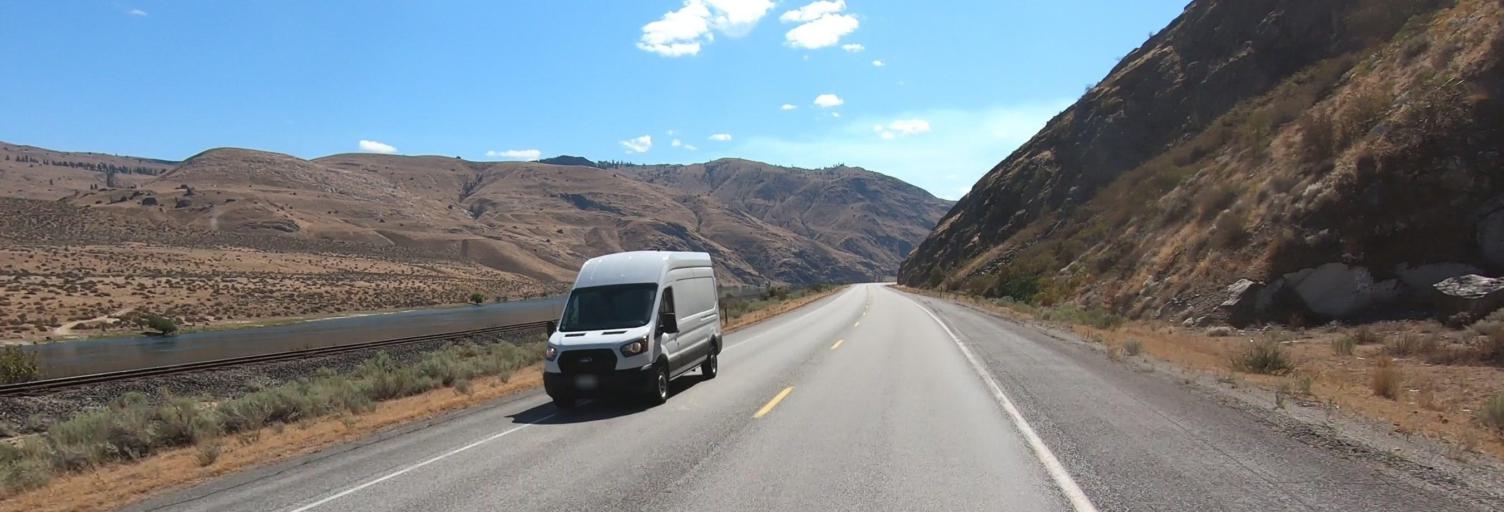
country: US
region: Washington
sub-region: Chelan County
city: Chelan
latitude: 47.8971
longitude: -119.9172
